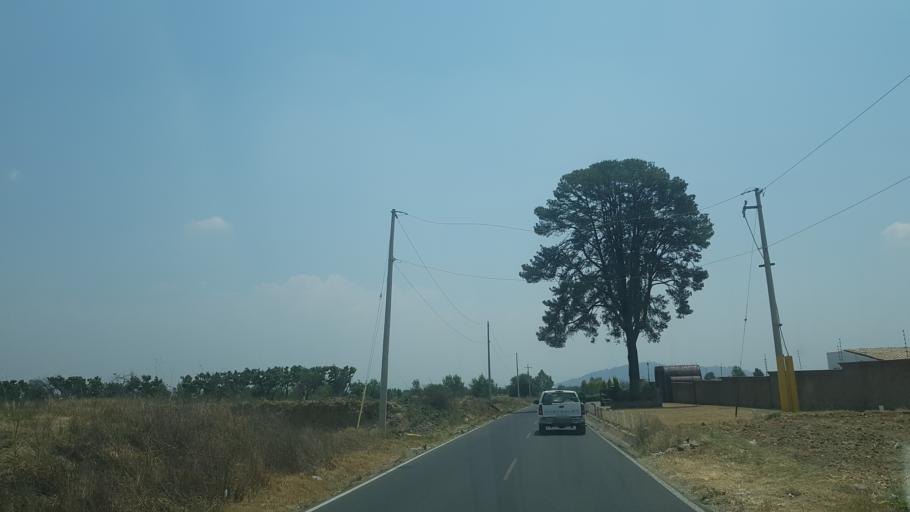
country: MX
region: Puebla
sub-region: San Jeronimo Tecuanipan
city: San Miguel Papaxtla
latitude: 19.0953
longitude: -98.4070
